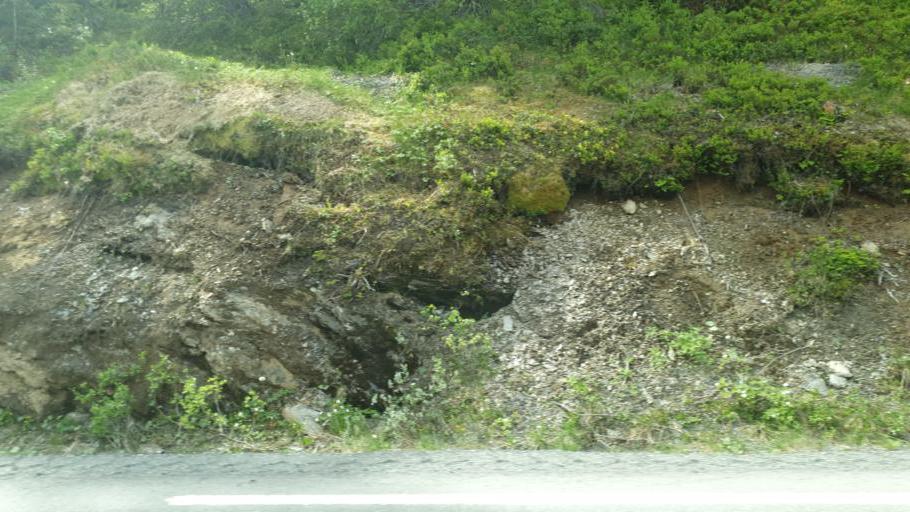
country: NO
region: Nord-Trondelag
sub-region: Leksvik
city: Leksvik
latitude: 63.6919
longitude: 10.5144
